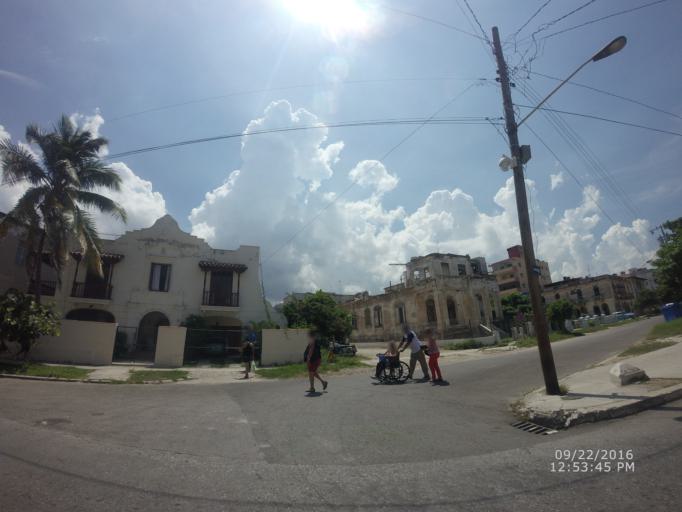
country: CU
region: La Habana
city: Havana
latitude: 23.1453
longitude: -82.3892
